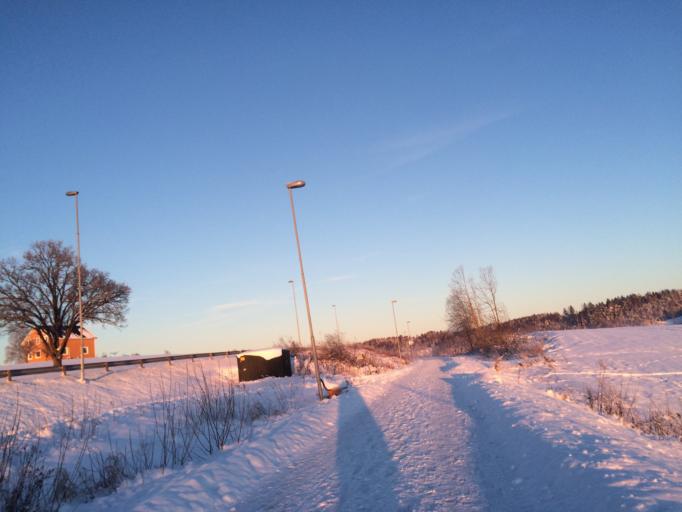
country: NO
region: Akershus
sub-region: Ski
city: Ski
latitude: 59.6944
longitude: 10.8288
